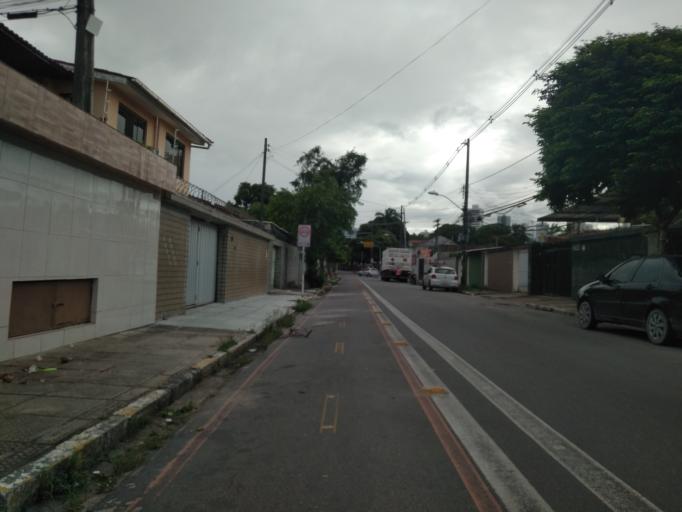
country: BR
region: Pernambuco
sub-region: Recife
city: Recife
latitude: -8.0316
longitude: -34.8846
